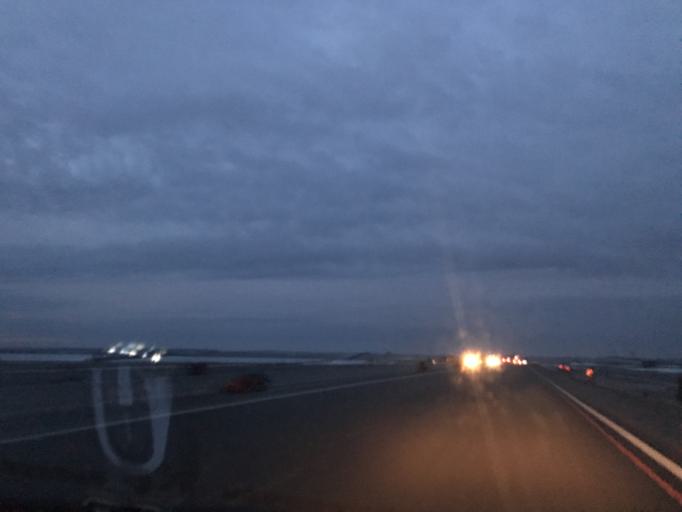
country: RU
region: Rostov
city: Samarskoye
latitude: 47.0151
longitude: 39.7346
